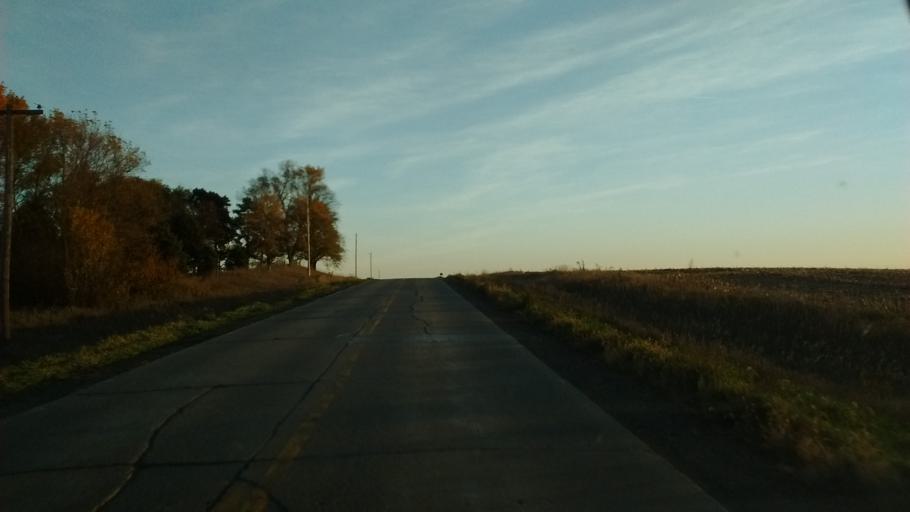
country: US
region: Iowa
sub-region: Plymouth County
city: Le Mars
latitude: 42.7541
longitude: -96.1555
